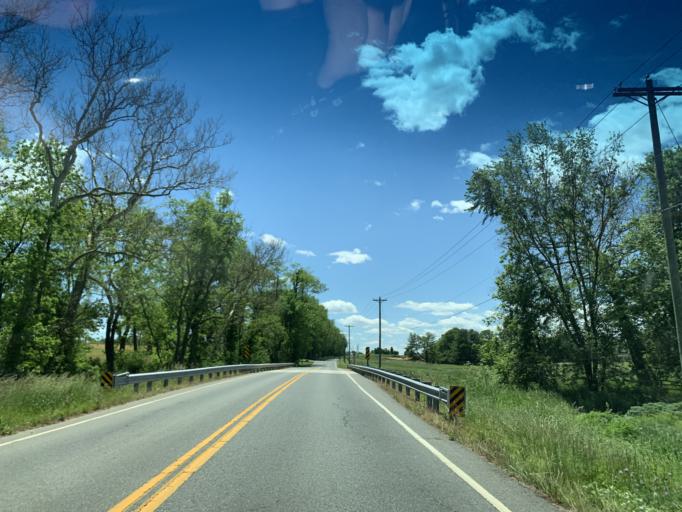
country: US
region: Maryland
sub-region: Cecil County
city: Rising Sun
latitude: 39.6894
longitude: -76.0072
